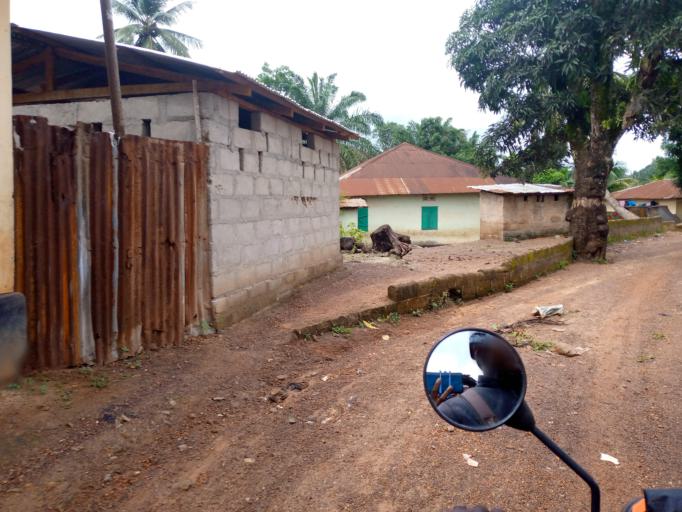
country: SL
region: Eastern Province
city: Kenema
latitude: 7.8643
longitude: -11.1891
